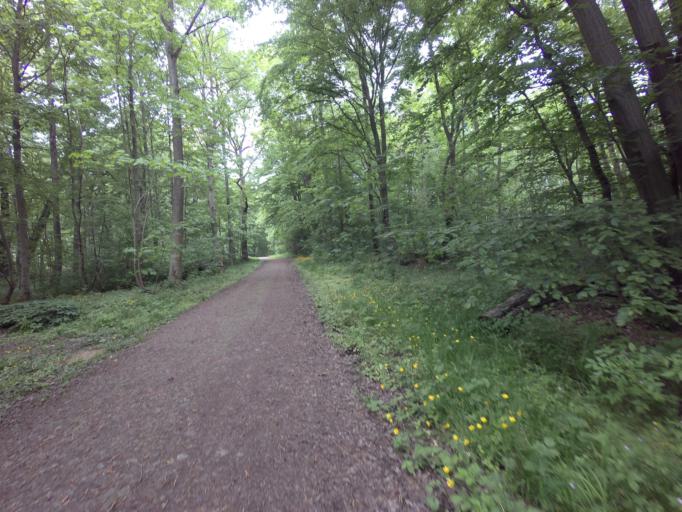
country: DE
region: Lower Saxony
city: Cremlingen
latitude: 52.2551
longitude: 10.5999
